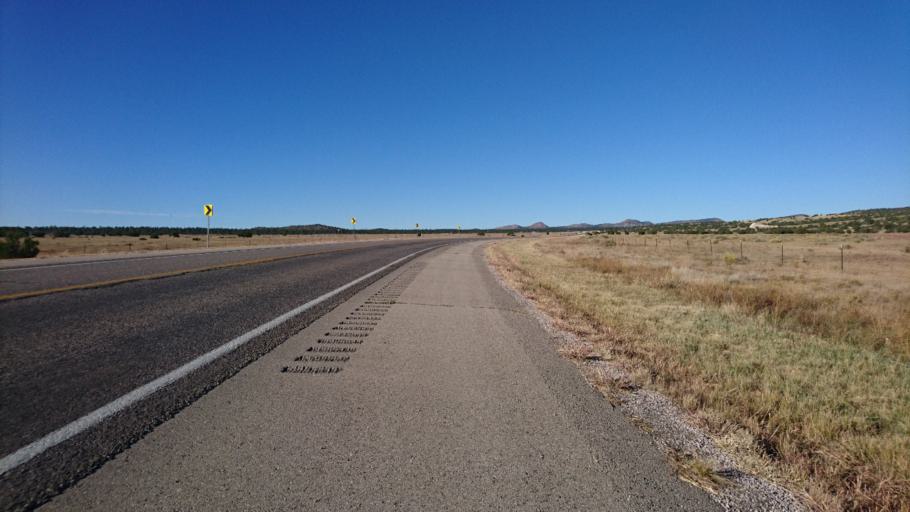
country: US
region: New Mexico
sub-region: Cibola County
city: Grants
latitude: 34.9620
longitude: -107.9158
